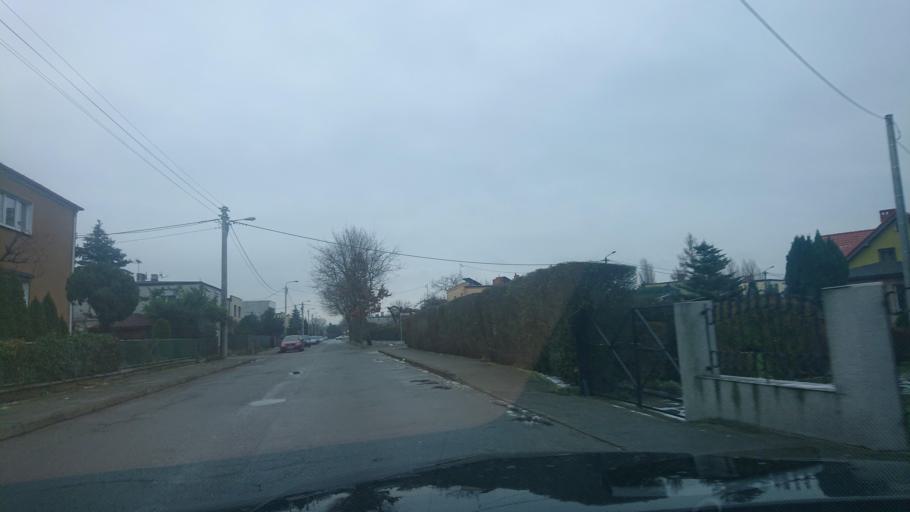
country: PL
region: Greater Poland Voivodeship
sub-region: Powiat gnieznienski
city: Gniezno
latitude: 52.5391
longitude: 17.5762
